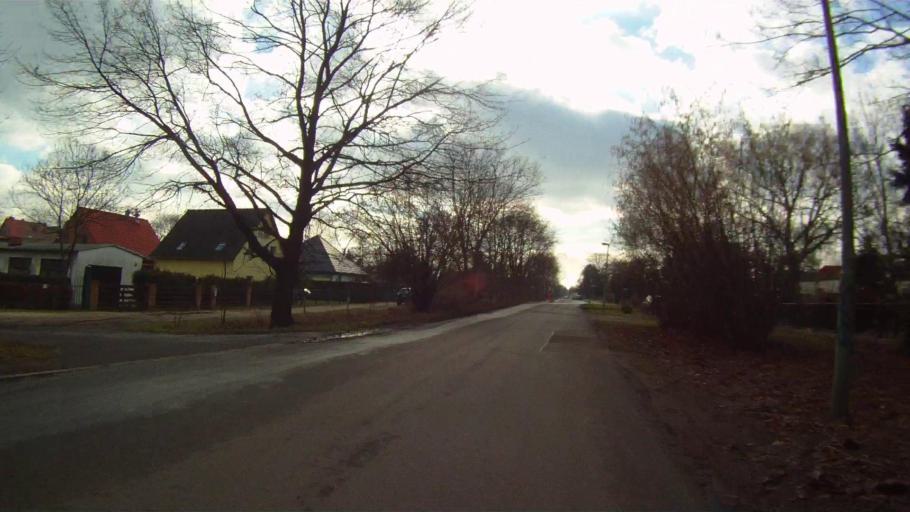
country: DE
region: Berlin
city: Biesdorf
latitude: 52.4989
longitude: 13.5554
